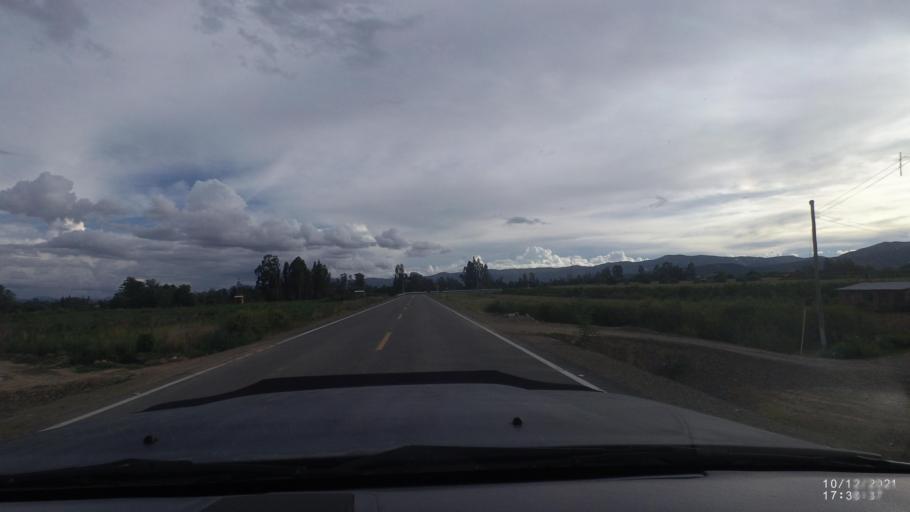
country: BO
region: Cochabamba
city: Tarata
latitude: -17.5719
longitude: -66.0097
